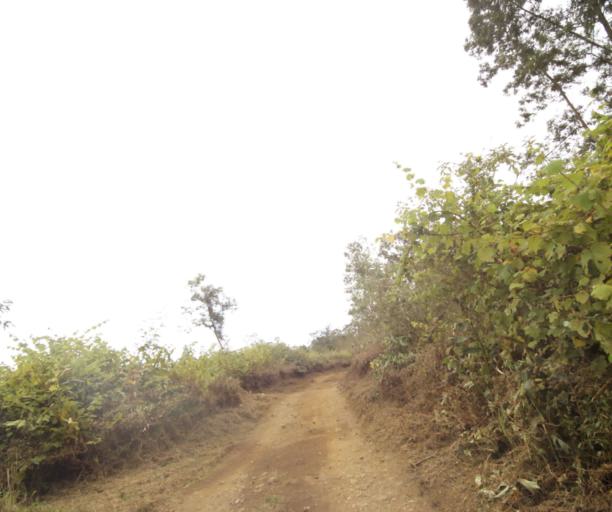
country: RE
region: Reunion
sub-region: Reunion
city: La Possession
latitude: -21.0130
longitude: 55.3586
